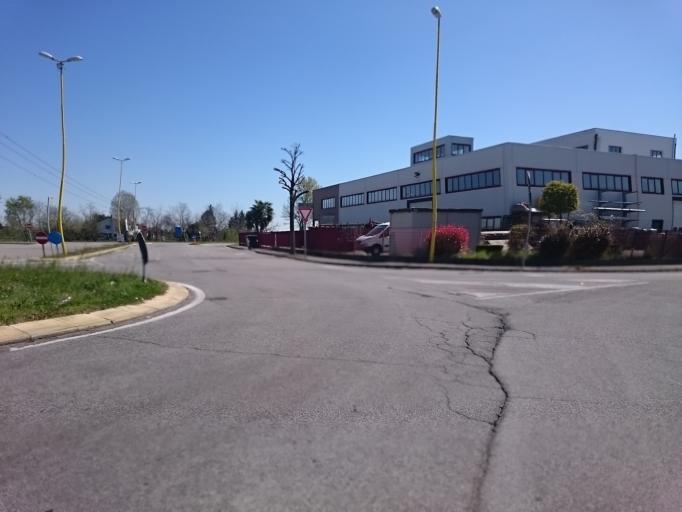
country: IT
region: Veneto
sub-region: Provincia di Padova
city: Ponte San Nicolo
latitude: 45.3553
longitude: 11.9309
